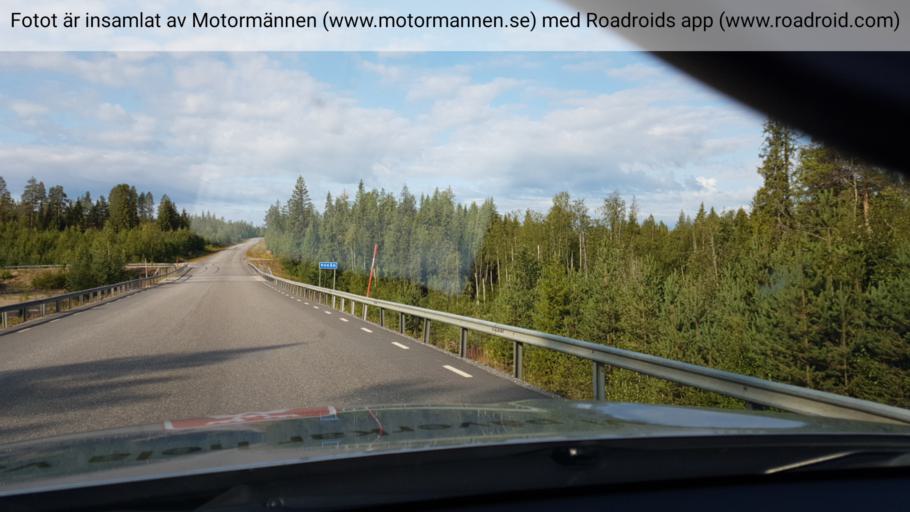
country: SE
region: Vaesterbotten
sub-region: Skelleftea Kommun
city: Storvik
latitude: 65.3346
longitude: 20.8581
